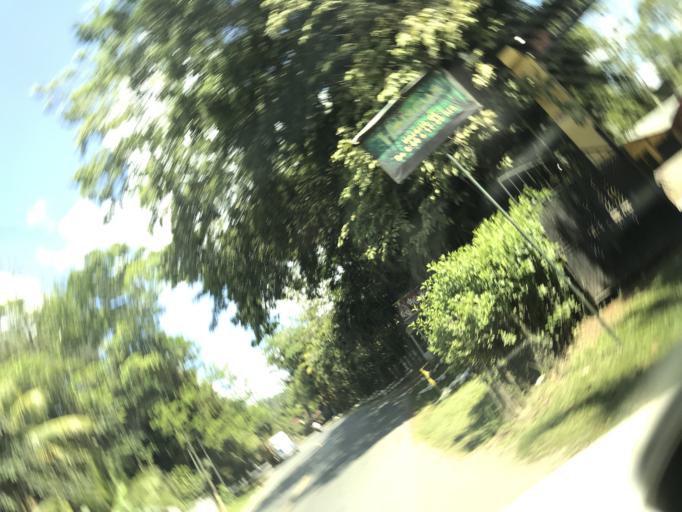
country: GT
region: Izabal
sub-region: Municipio de Puerto Barrios
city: Puerto Barrios
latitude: 15.6499
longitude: -88.5489
